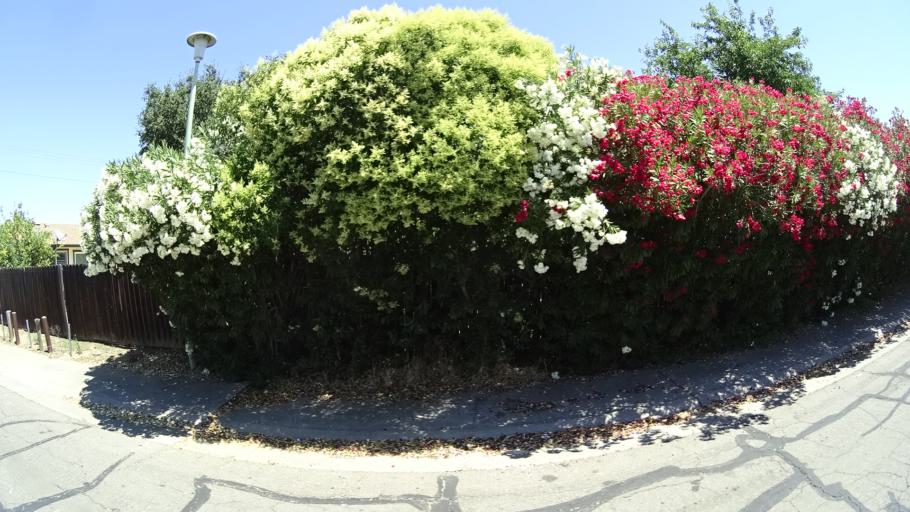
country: US
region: California
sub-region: Sacramento County
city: Parkway
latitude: 38.5332
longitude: -121.4821
